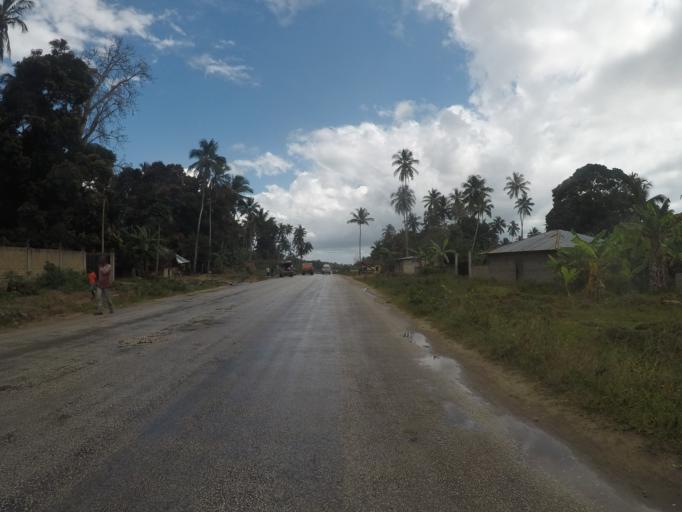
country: TZ
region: Zanzibar Central/South
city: Koani
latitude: -6.0279
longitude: 39.2381
